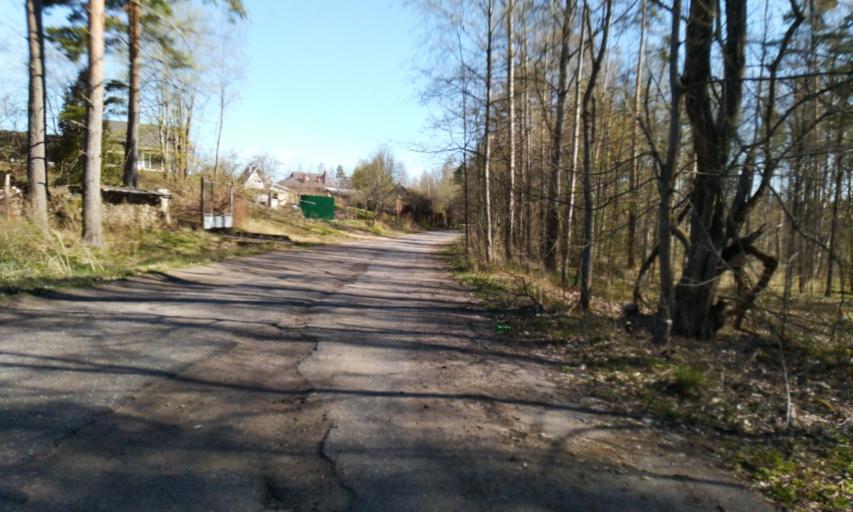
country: RU
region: Leningrad
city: Garbolovo
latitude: 60.3885
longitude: 30.4857
